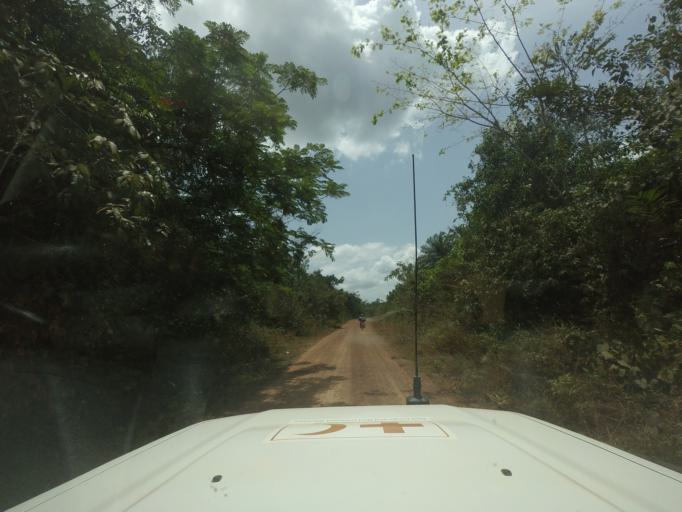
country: LR
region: Bong
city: Gbarnga
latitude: 7.1541
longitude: -9.2155
